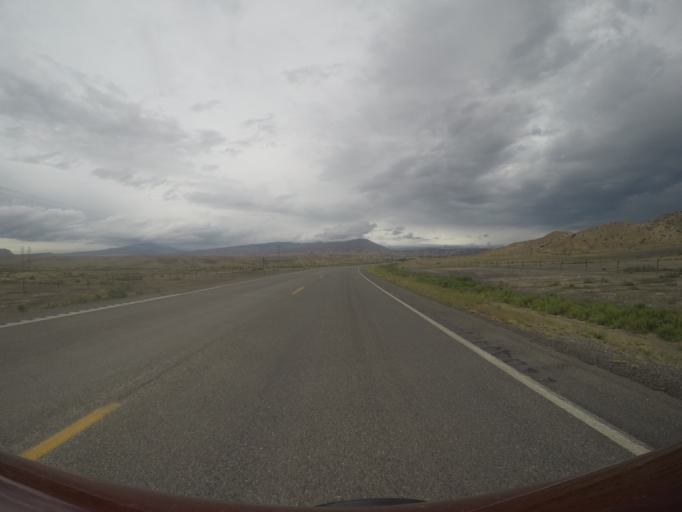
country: US
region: Wyoming
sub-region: Big Horn County
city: Lovell
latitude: 44.9481
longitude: -108.2970
